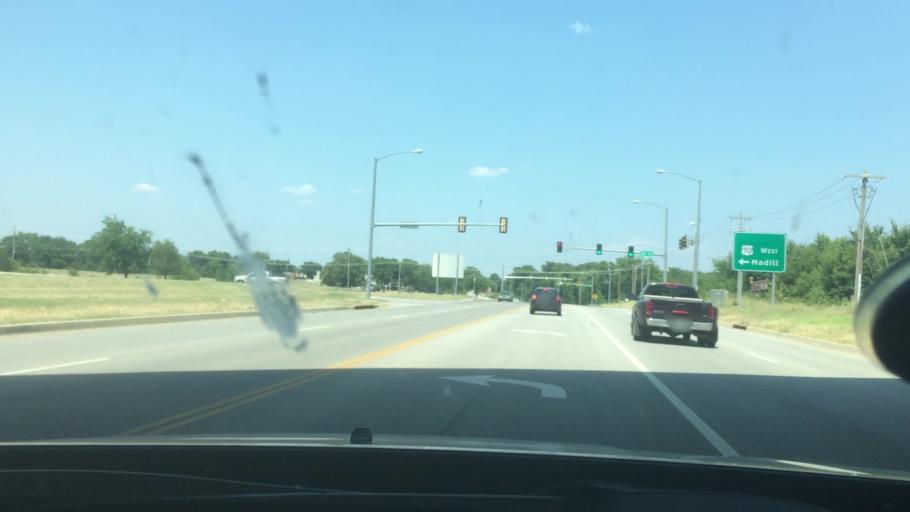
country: US
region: Oklahoma
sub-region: Bryan County
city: Durant
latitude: 33.9656
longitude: -96.3957
